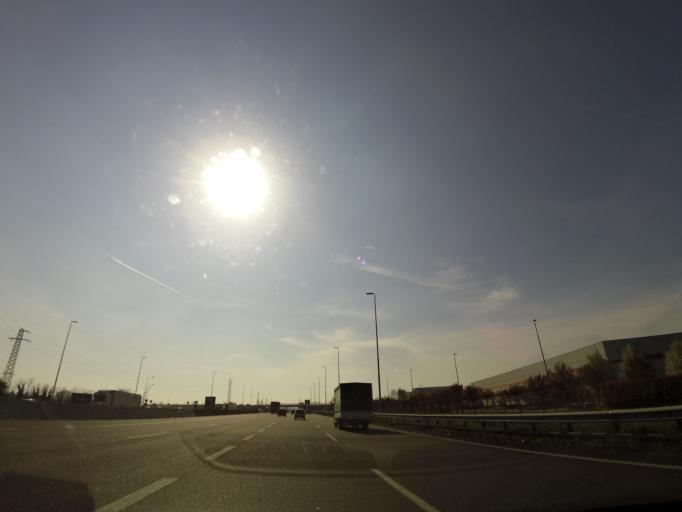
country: IT
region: Lombardy
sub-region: Citta metropolitana di Milano
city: Chiaravalle
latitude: 45.4444
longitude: 9.2401
